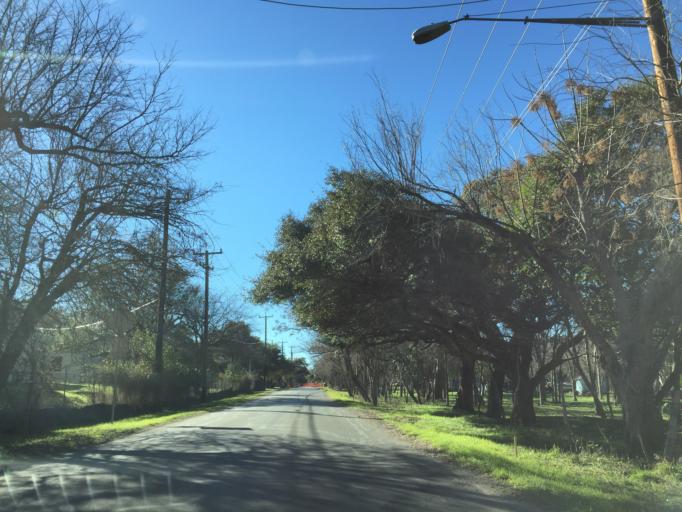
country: US
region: Texas
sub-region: Bexar County
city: Castle Hills
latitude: 29.5552
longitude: -98.4957
